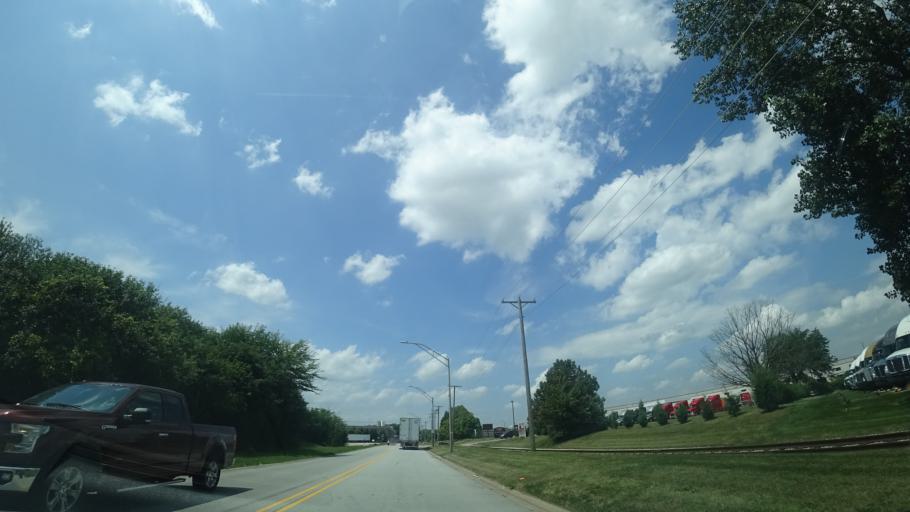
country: US
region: Illinois
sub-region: Cook County
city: Crestwood
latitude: 41.6710
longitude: -87.7560
